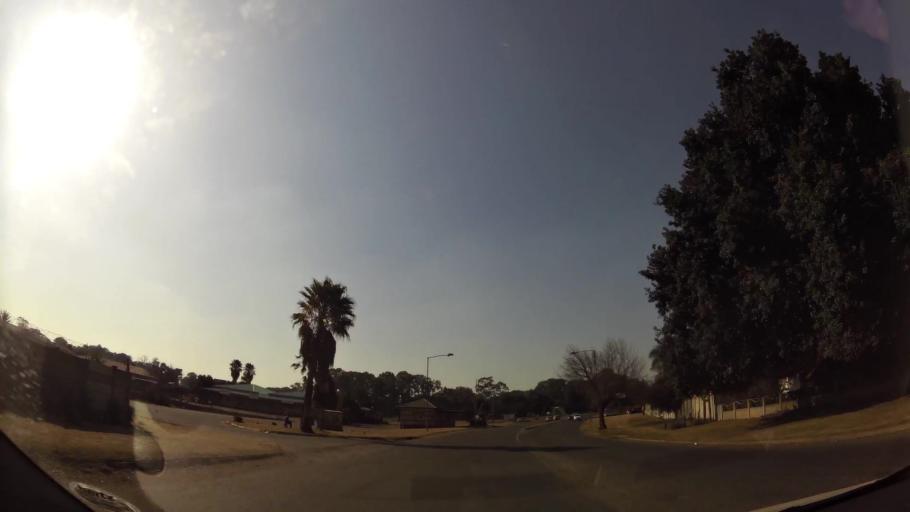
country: ZA
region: Gauteng
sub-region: West Rand District Municipality
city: Randfontein
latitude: -26.1754
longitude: 27.6939
